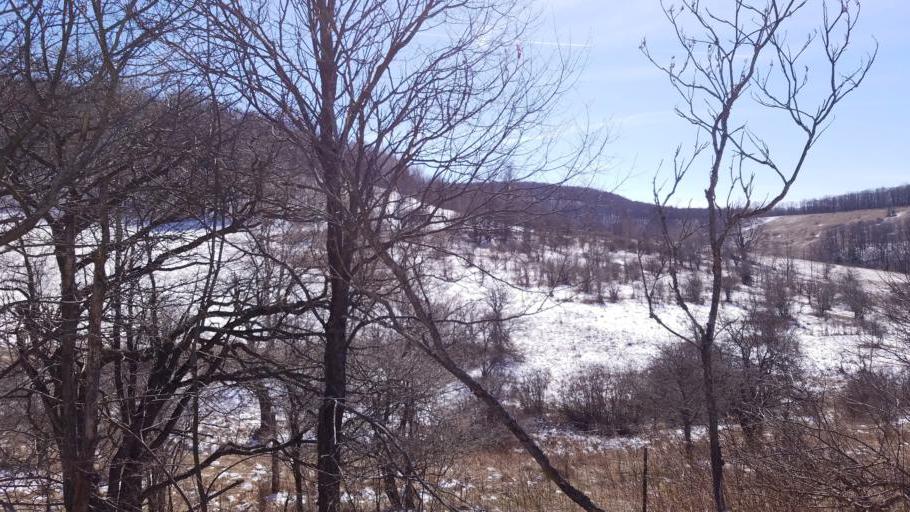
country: US
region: New York
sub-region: Allegany County
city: Andover
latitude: 41.9376
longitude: -77.7983
